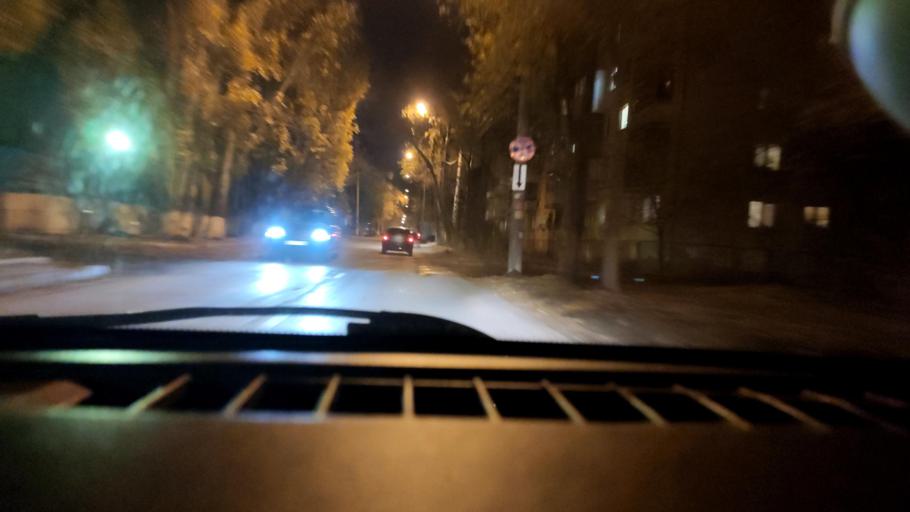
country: RU
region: Samara
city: Samara
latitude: 53.1957
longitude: 50.1837
